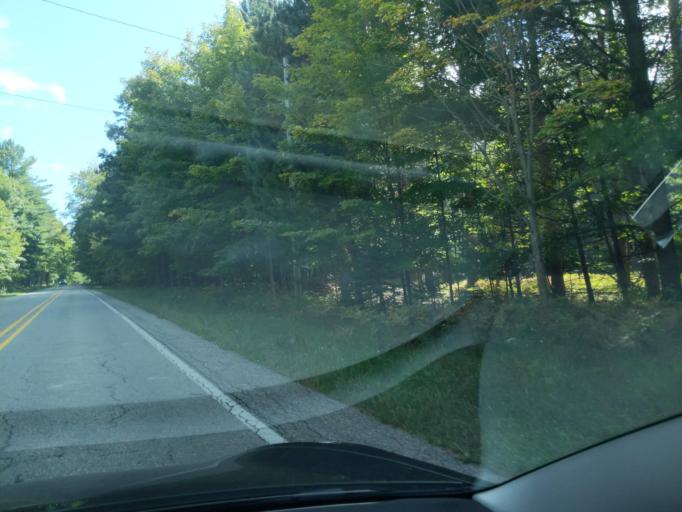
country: US
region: Michigan
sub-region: Antrim County
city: Bellaire
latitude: 45.0737
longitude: -85.3194
